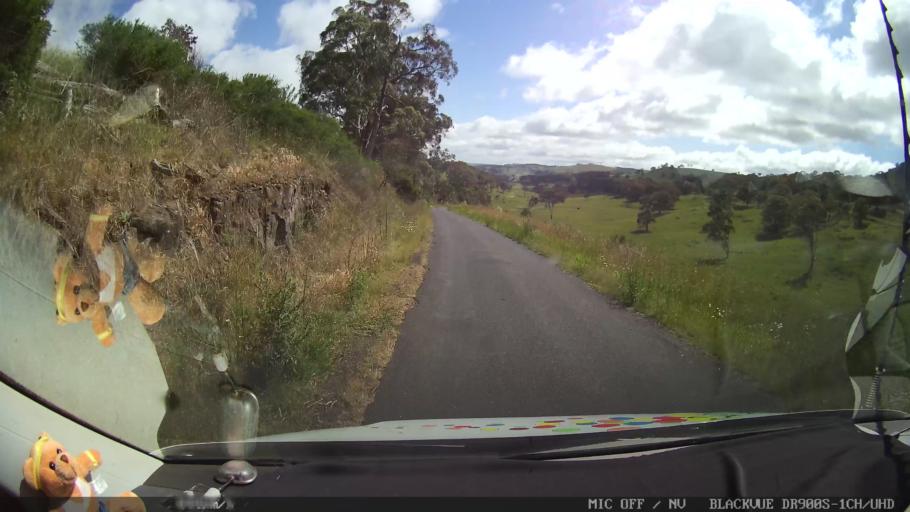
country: AU
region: New South Wales
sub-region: Guyra
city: Guyra
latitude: -30.0018
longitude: 151.6706
